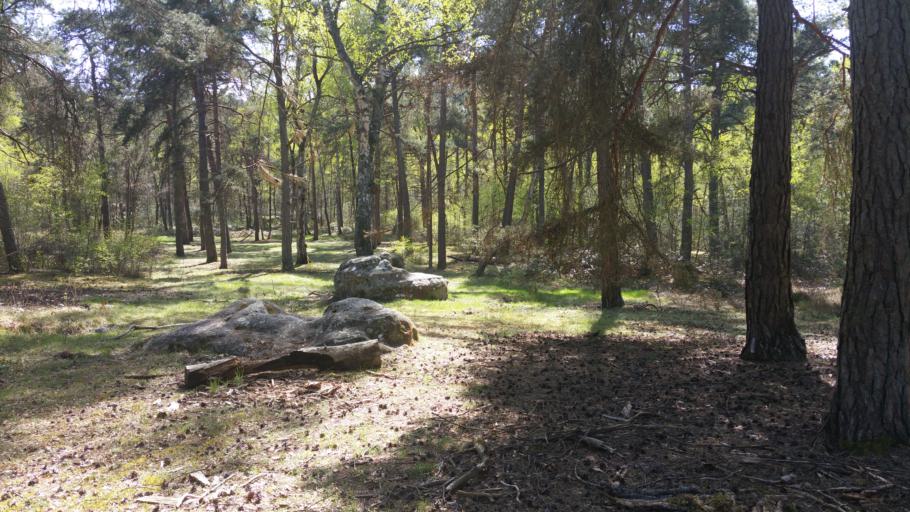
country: FR
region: Ile-de-France
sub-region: Departement de Seine-et-Marne
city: Arbonne-la-Foret
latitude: 48.3980
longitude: 2.5448
